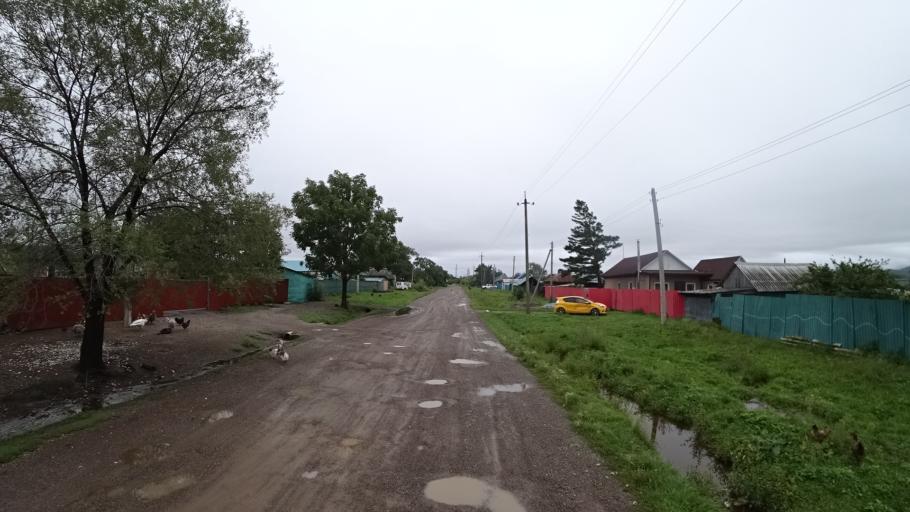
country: RU
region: Primorskiy
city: Monastyrishche
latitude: 44.1971
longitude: 132.4589
